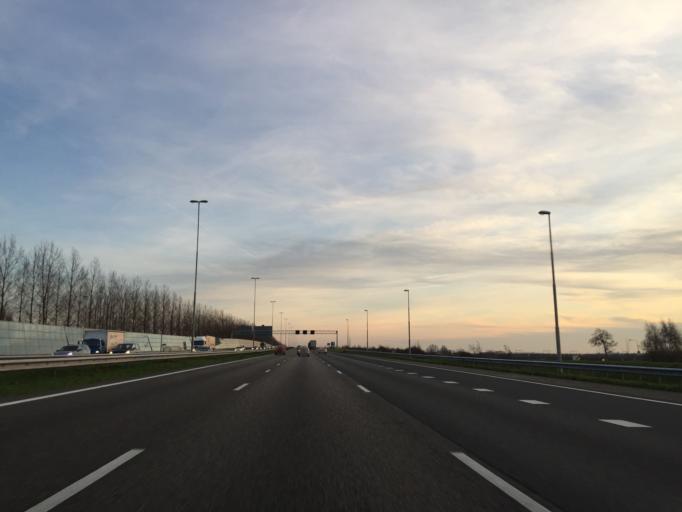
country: NL
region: North Brabant
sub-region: Gemeente Made en Drimmelen
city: Made
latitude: 51.6799
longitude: 4.6654
